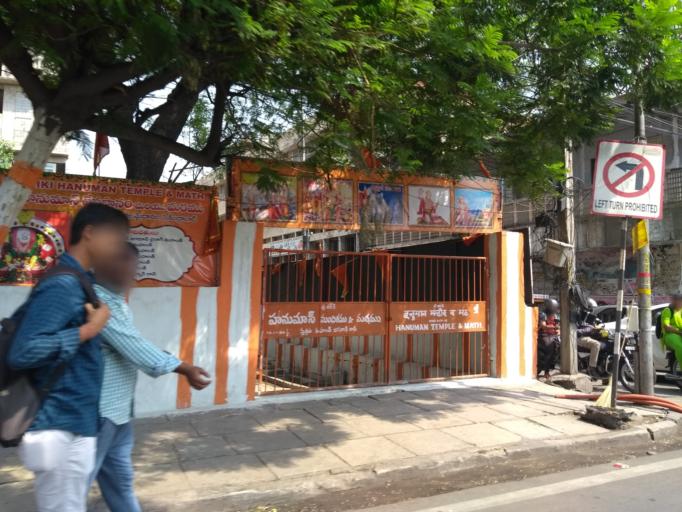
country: IN
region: Telangana
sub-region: Hyderabad
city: Malkajgiri
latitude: 17.4284
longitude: 78.4878
